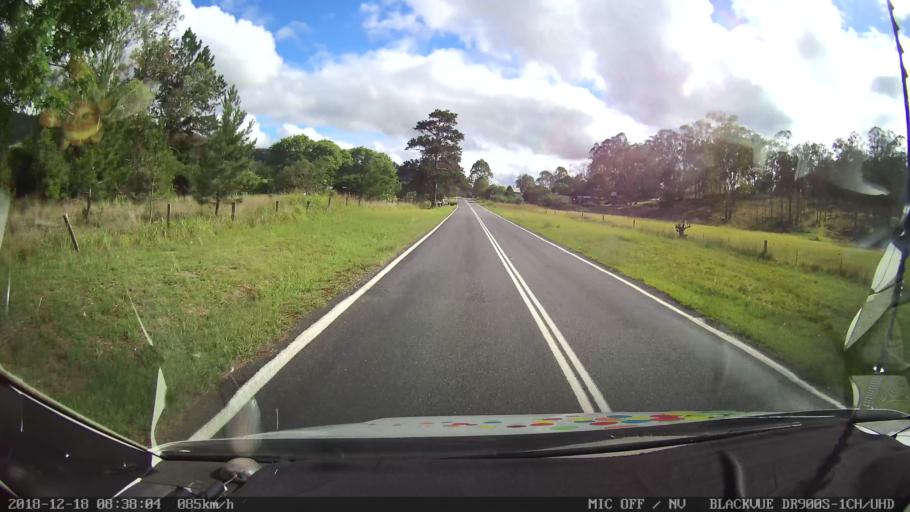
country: AU
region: New South Wales
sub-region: Kyogle
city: Kyogle
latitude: -28.2591
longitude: 152.8241
